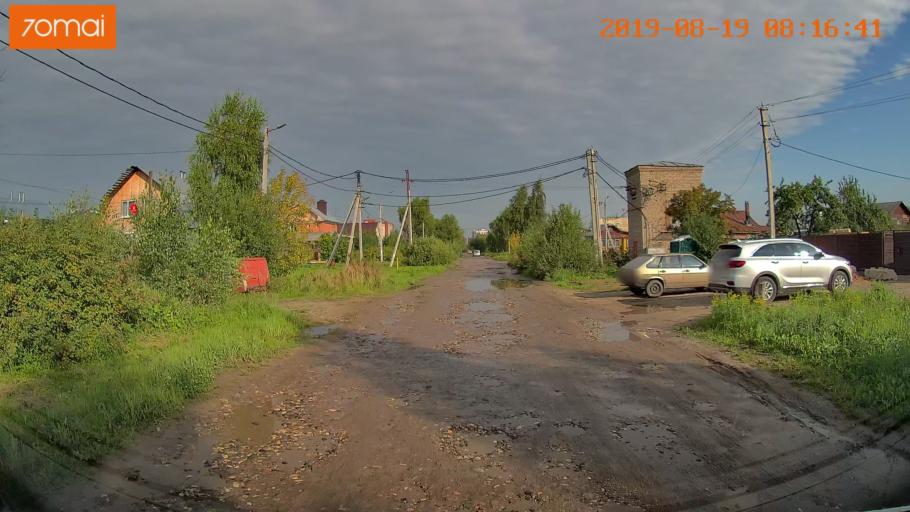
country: RU
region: Ivanovo
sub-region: Gorod Ivanovo
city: Ivanovo
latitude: 56.9750
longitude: 40.9986
